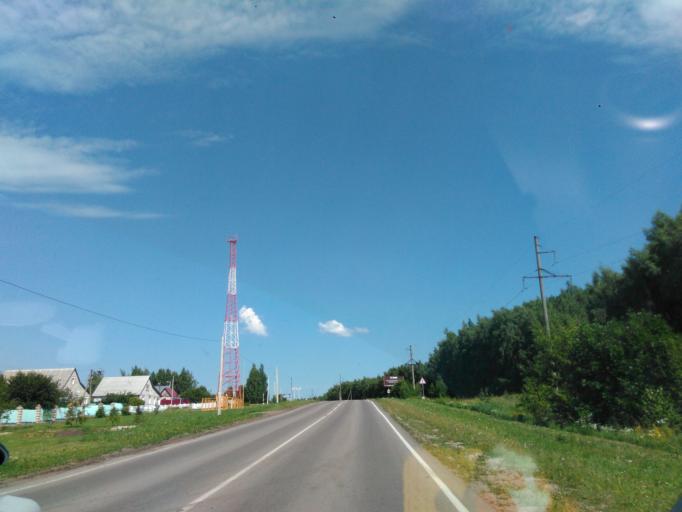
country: RU
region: Penza
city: Belinskiy
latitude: 52.9672
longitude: 43.4528
